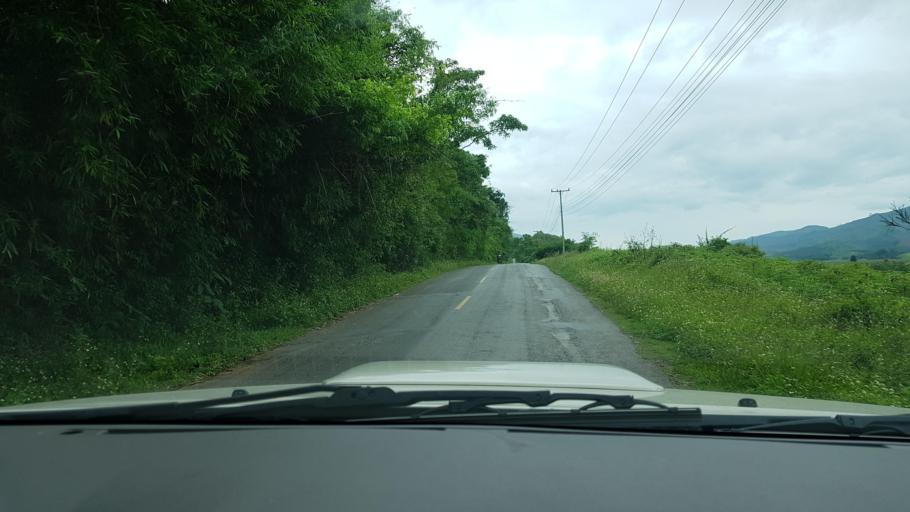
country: LA
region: Loungnamtha
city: Muang Nale
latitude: 20.2788
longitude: 101.6095
